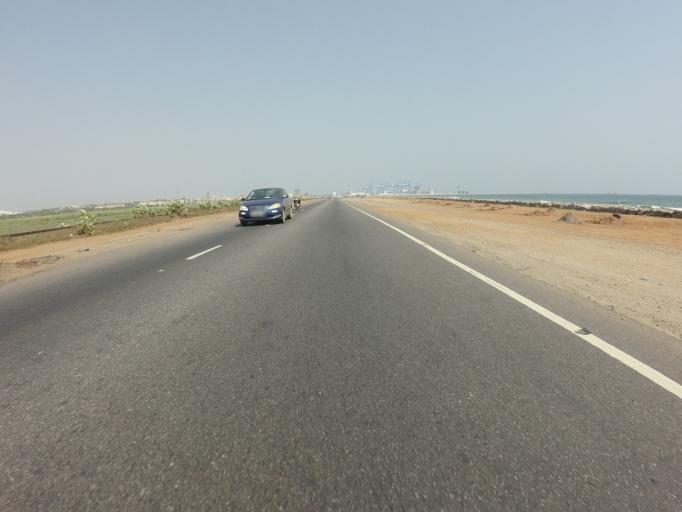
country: GH
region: Greater Accra
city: Nungua
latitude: 5.6132
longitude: -0.0362
